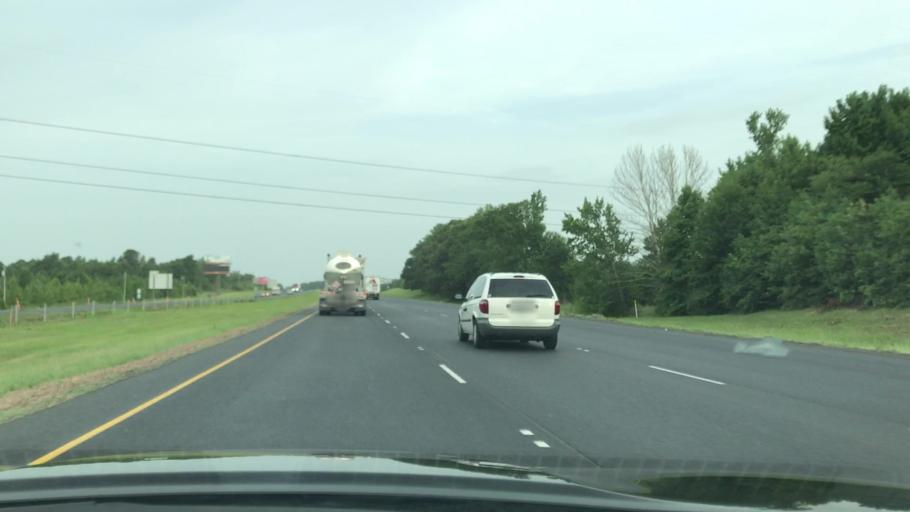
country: US
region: Louisiana
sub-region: Caddo Parish
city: Greenwood
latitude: 32.4482
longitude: -93.9844
